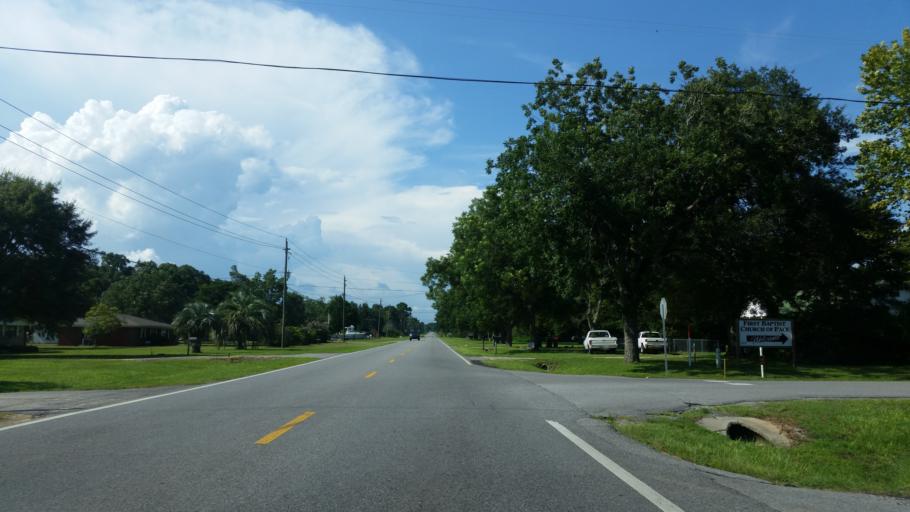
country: US
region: Florida
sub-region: Santa Rosa County
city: Pace
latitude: 30.6038
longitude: -87.1615
